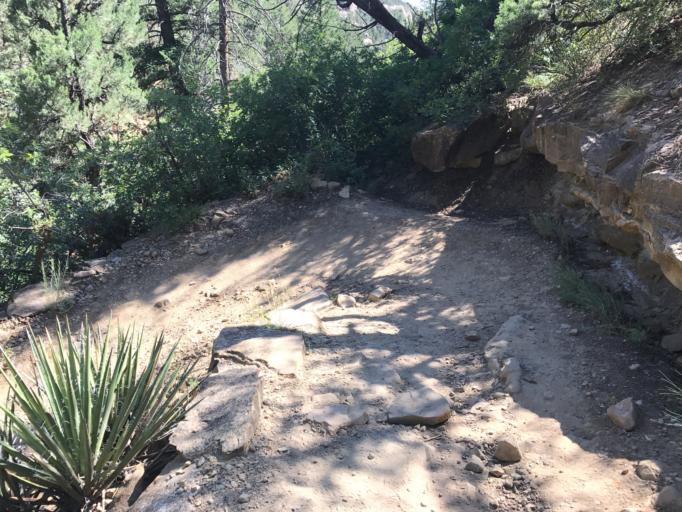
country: US
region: Colorado
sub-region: Montezuma County
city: Cortez
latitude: 37.1834
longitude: -108.4877
